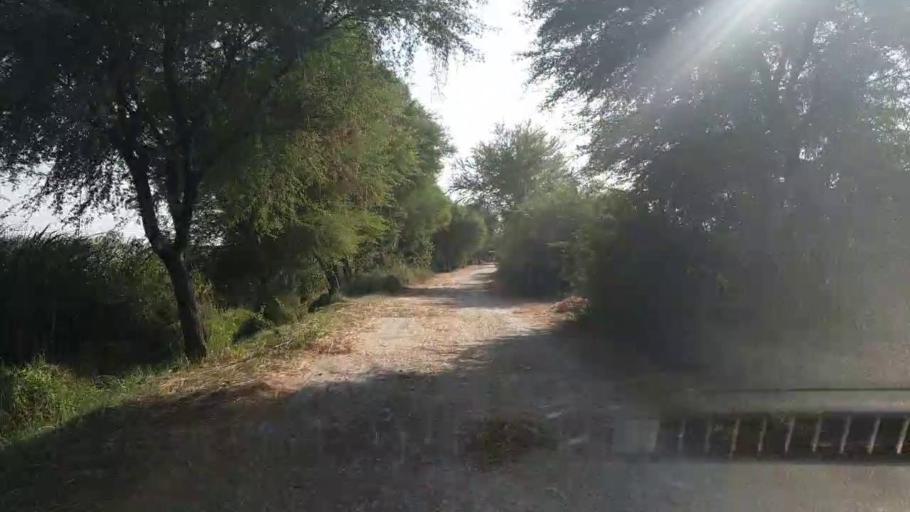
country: PK
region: Sindh
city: Matli
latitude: 25.0171
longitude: 68.7405
